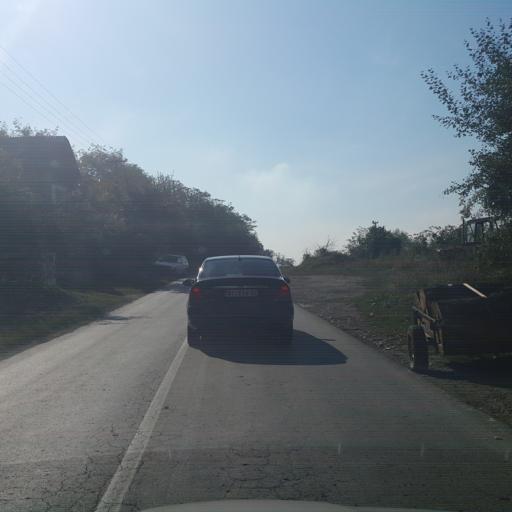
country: RS
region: Central Serbia
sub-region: Pirotski Okrug
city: Pirot
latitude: 43.1892
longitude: 22.5695
